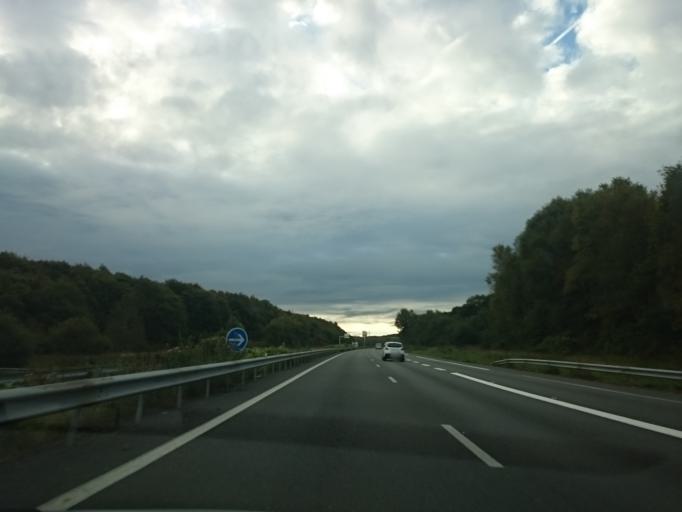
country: FR
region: Brittany
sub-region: Departement du Finistere
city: Le Faou
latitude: 48.2957
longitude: -4.1690
